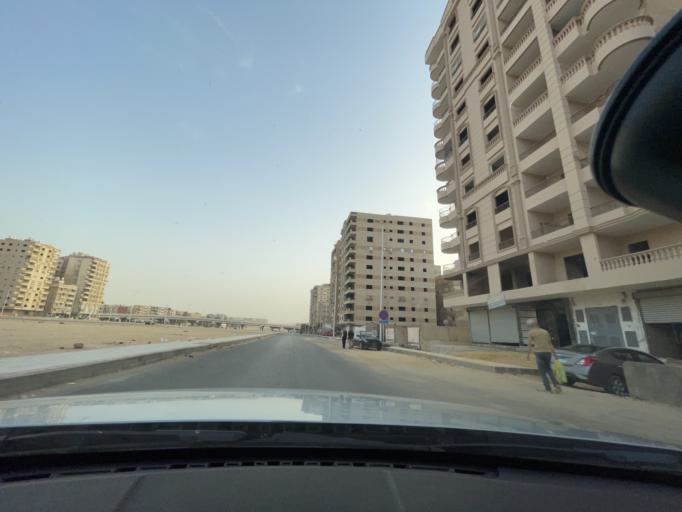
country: EG
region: Muhafazat al Qahirah
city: Cairo
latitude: 30.0506
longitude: 31.3678
